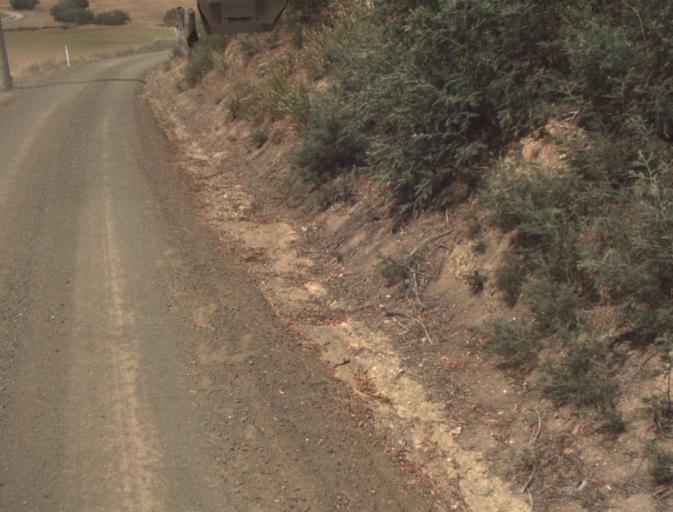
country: AU
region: Tasmania
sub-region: Launceston
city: Mayfield
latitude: -41.2096
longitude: 147.1412
